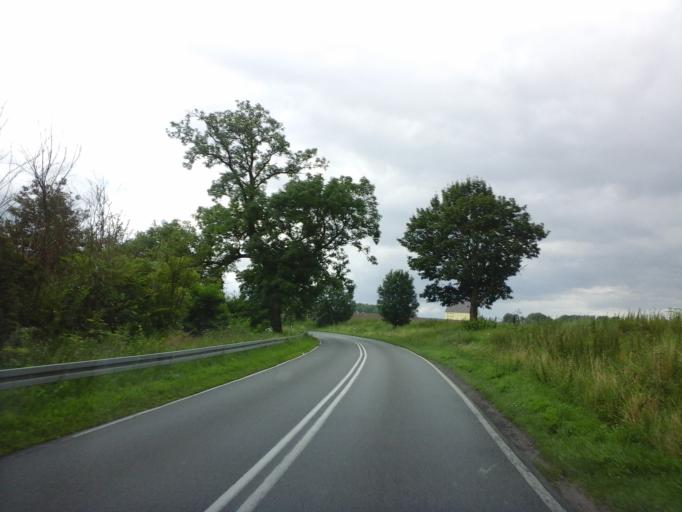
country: PL
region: West Pomeranian Voivodeship
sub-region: Powiat choszczenski
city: Choszczno
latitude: 53.1472
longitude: 15.4506
